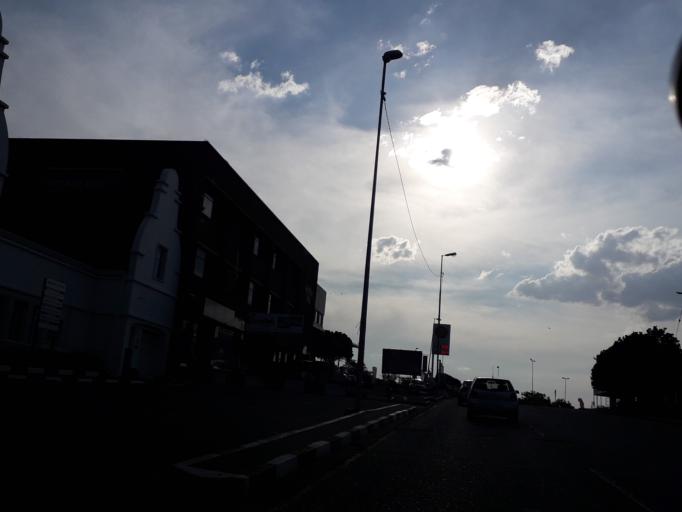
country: ZA
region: Gauteng
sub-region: City of Johannesburg Metropolitan Municipality
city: Johannesburg
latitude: -26.1163
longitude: 28.0030
